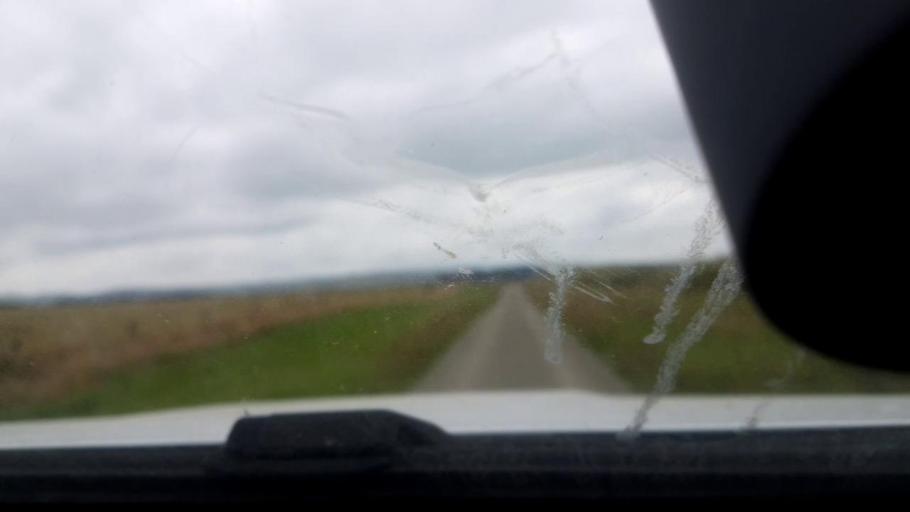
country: NZ
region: Canterbury
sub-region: Timaru District
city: Pleasant Point
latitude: -44.2348
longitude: 171.1680
